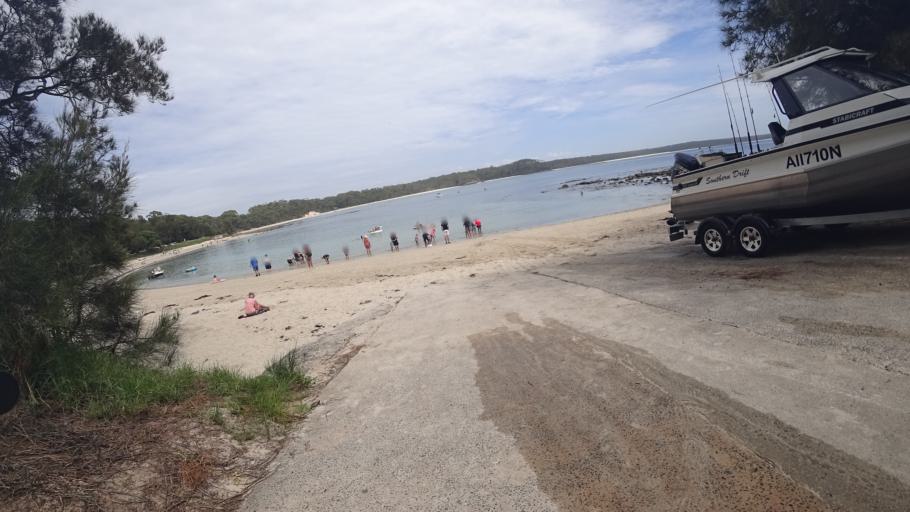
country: AU
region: New South Wales
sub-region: Shoalhaven Shire
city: Milton
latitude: -35.2449
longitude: 150.5392
